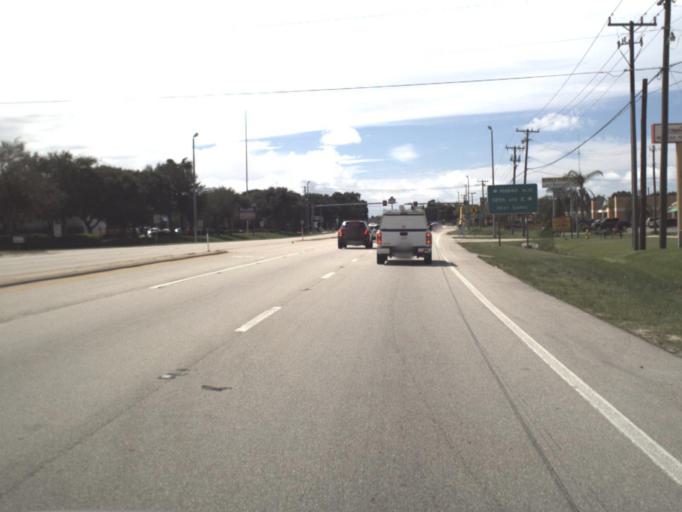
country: US
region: Florida
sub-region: Manatee County
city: Memphis
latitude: 27.5212
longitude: -82.5499
